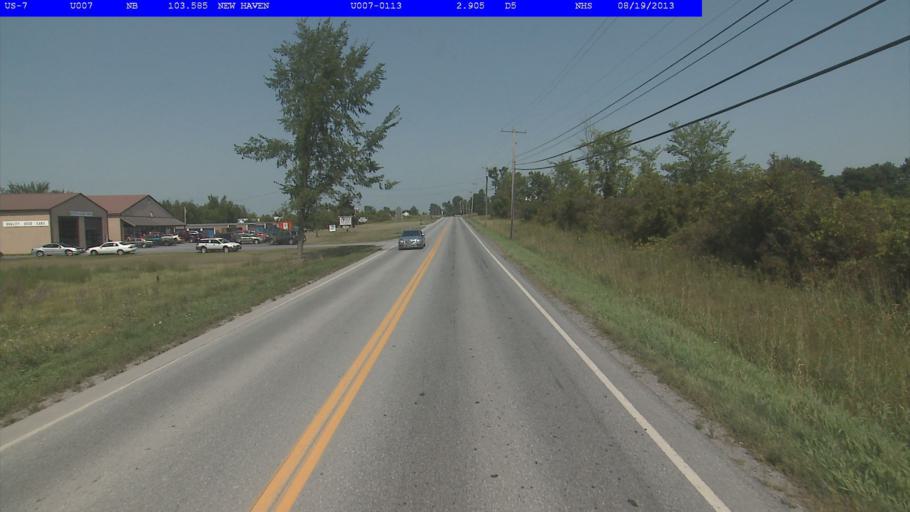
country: US
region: Vermont
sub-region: Addison County
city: Middlebury (village)
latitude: 44.0873
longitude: -73.1754
